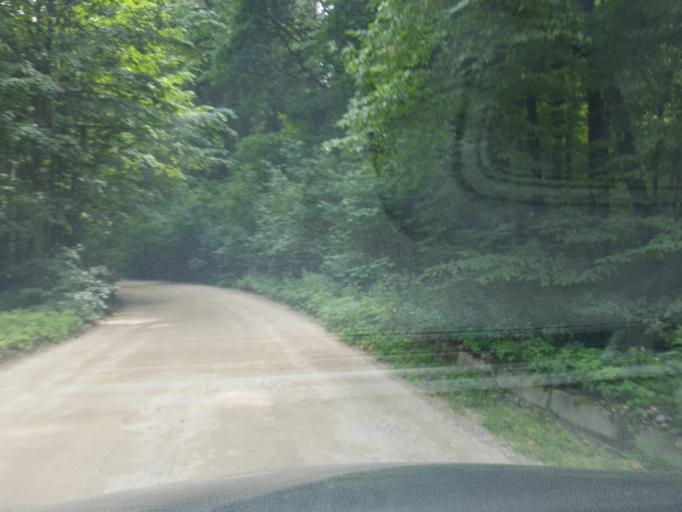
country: LT
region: Alytaus apskritis
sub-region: Alytus
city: Alytus
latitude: 54.3779
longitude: 24.0422
